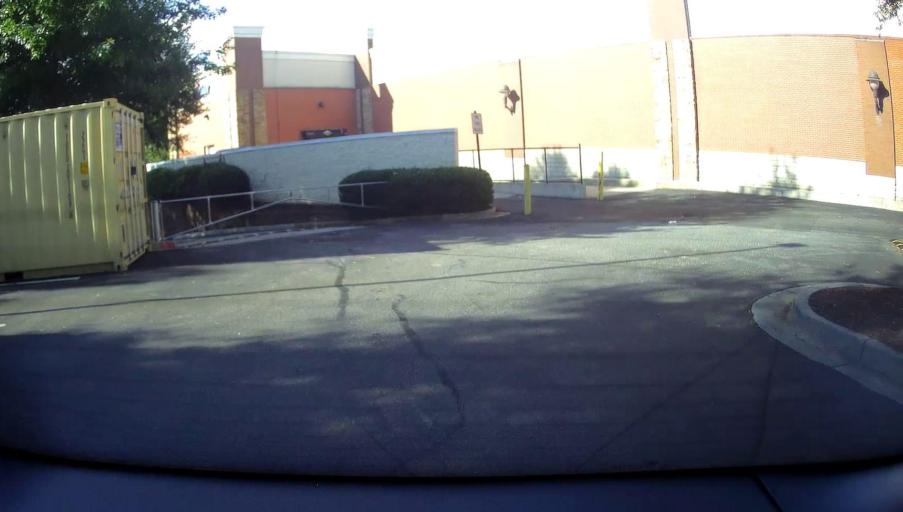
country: US
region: Georgia
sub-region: Fayette County
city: Peachtree City
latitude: 33.3983
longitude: -84.5972
